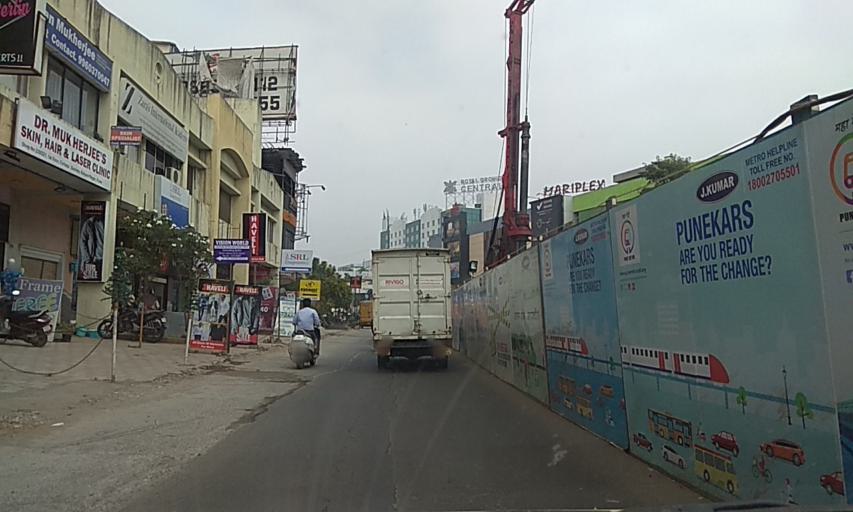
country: IN
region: Maharashtra
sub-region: Pune Division
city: Shivaji Nagar
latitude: 18.5445
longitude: 73.9056
